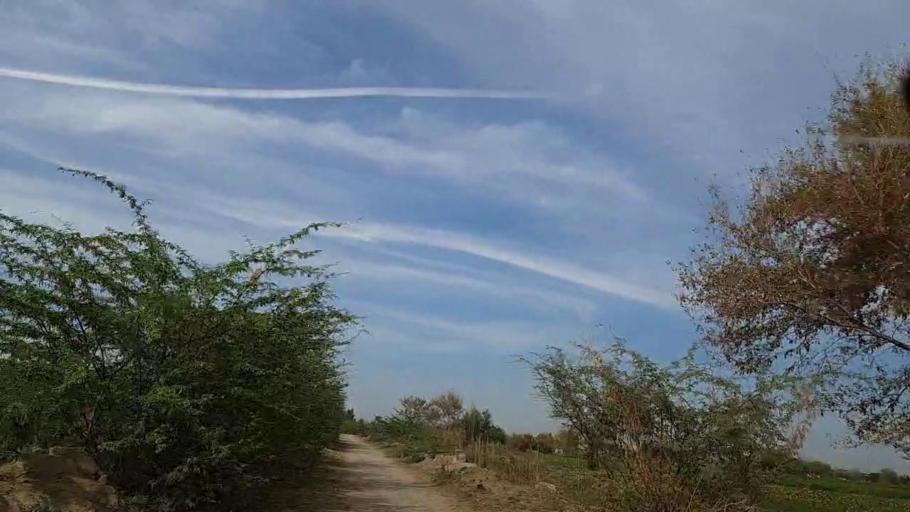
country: PK
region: Sindh
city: Dhoro Naro
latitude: 25.5153
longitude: 69.5287
